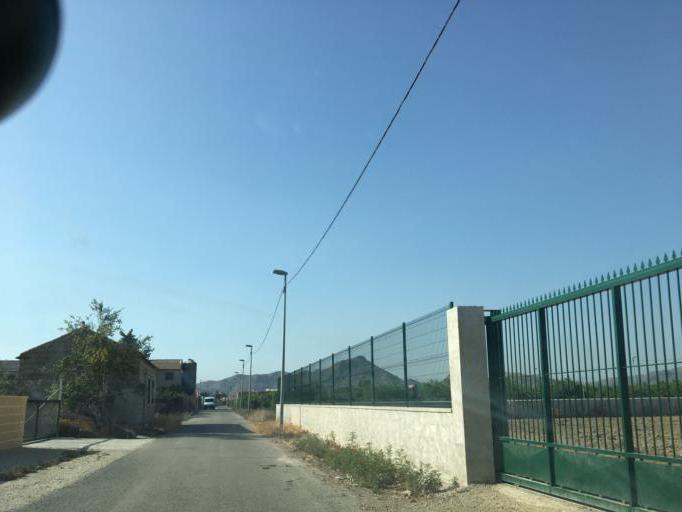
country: ES
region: Murcia
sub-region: Murcia
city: Santomera
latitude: 38.0299
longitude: -1.0568
